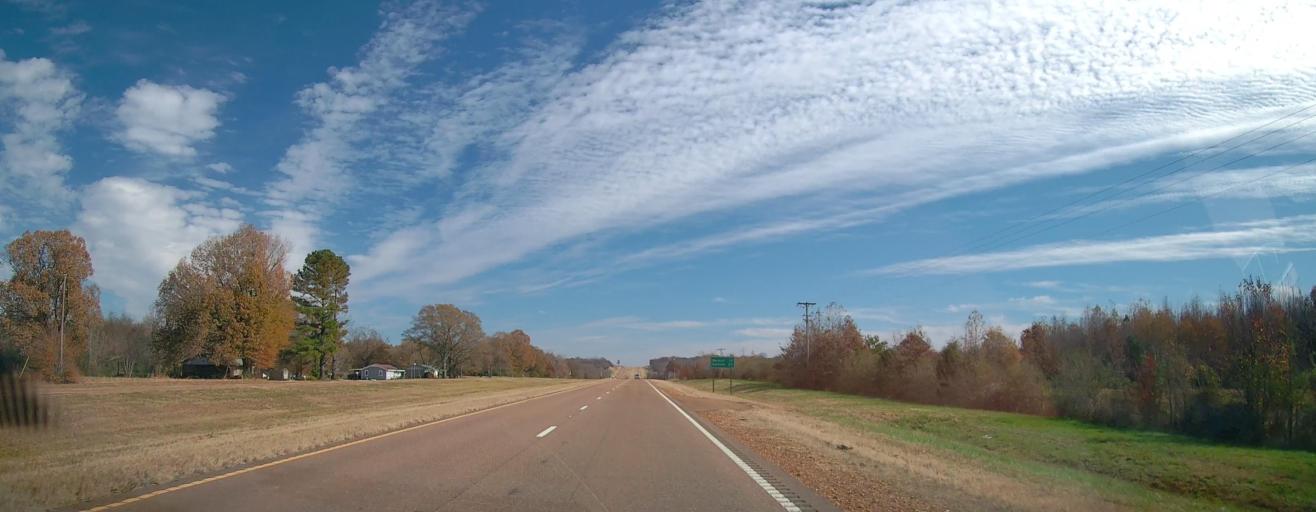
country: US
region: Mississippi
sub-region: Benton County
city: Ashland
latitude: 34.9461
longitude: -89.2083
